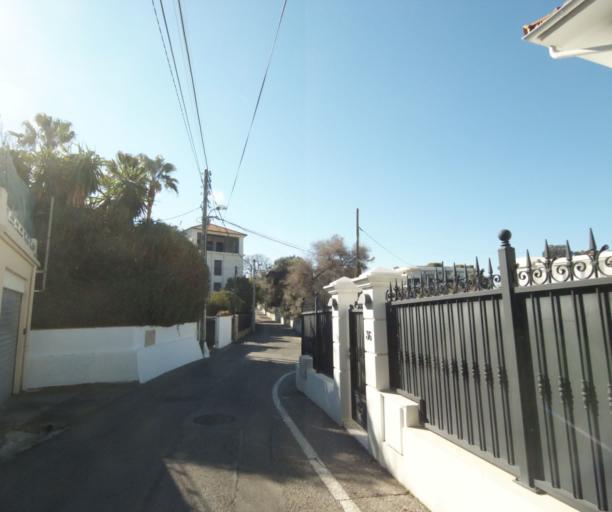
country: FR
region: Provence-Alpes-Cote d'Azur
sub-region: Departement des Alpes-Maritimes
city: Antibes
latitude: 43.5666
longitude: 7.1210
